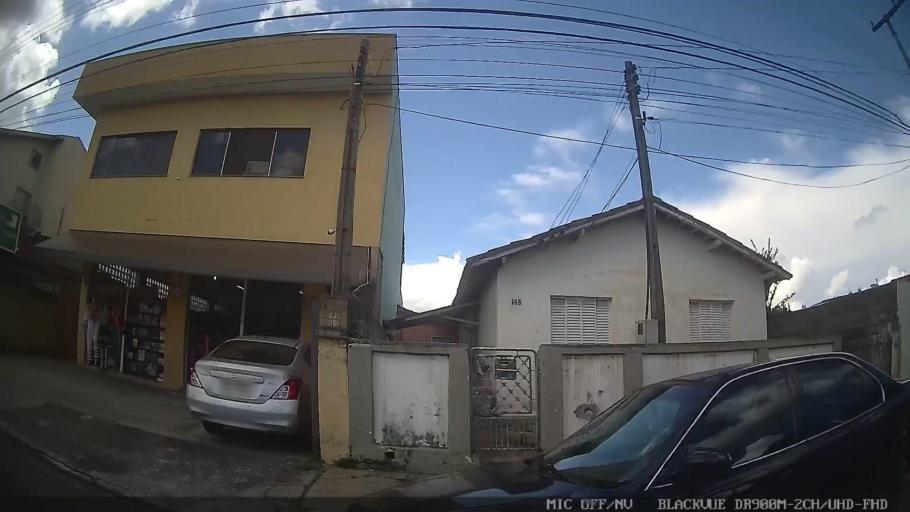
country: BR
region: Sao Paulo
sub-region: Atibaia
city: Atibaia
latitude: -23.1212
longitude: -46.5591
